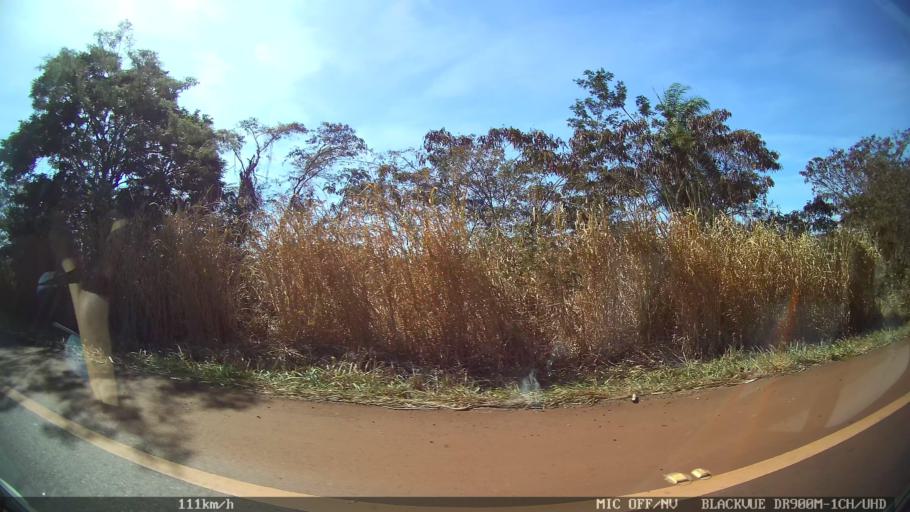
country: BR
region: Sao Paulo
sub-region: Sao Joaquim Da Barra
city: Sao Joaquim da Barra
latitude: -20.5287
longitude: -47.8340
